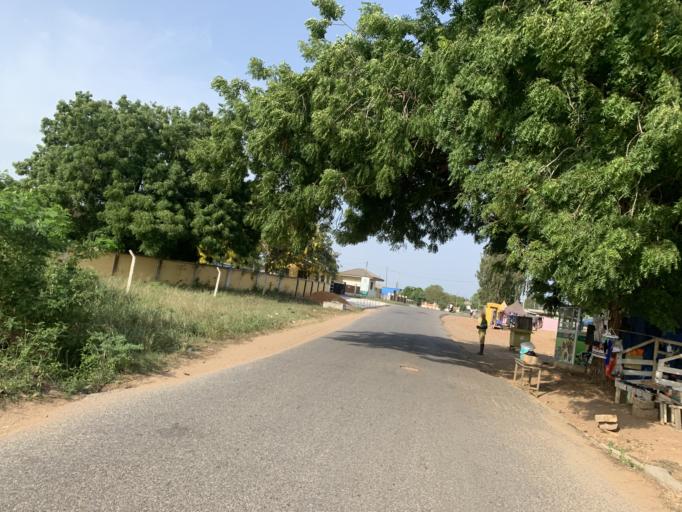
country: GH
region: Central
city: Winneba
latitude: 5.3705
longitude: -0.6428
